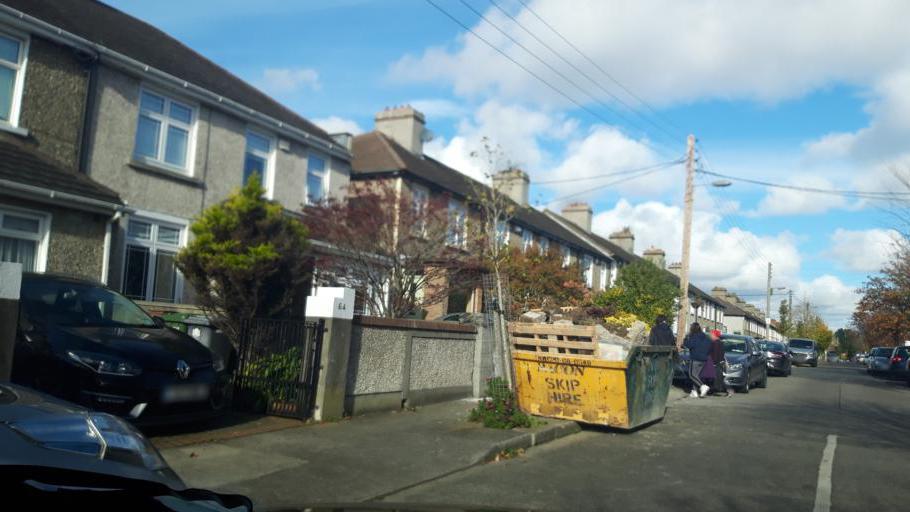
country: IE
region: Leinster
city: Marino
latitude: 53.3749
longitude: -6.2262
